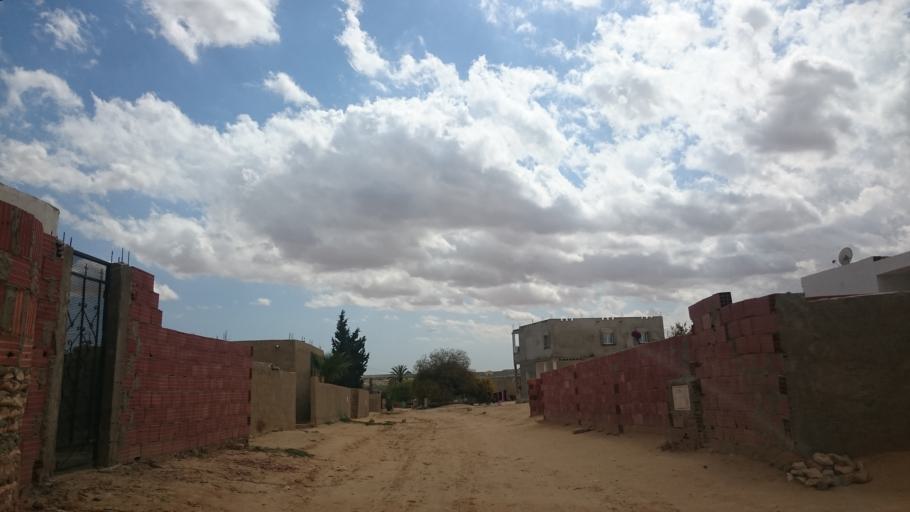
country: TN
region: Safaqis
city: Sfax
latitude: 34.7458
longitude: 10.4846
